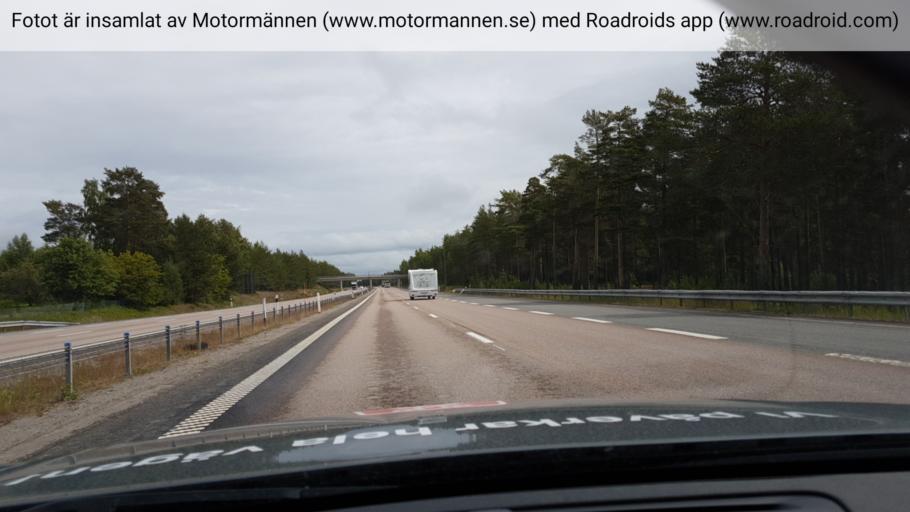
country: SE
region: Vaesternorrland
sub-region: Timra Kommun
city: Timra
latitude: 62.4995
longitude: 17.3423
